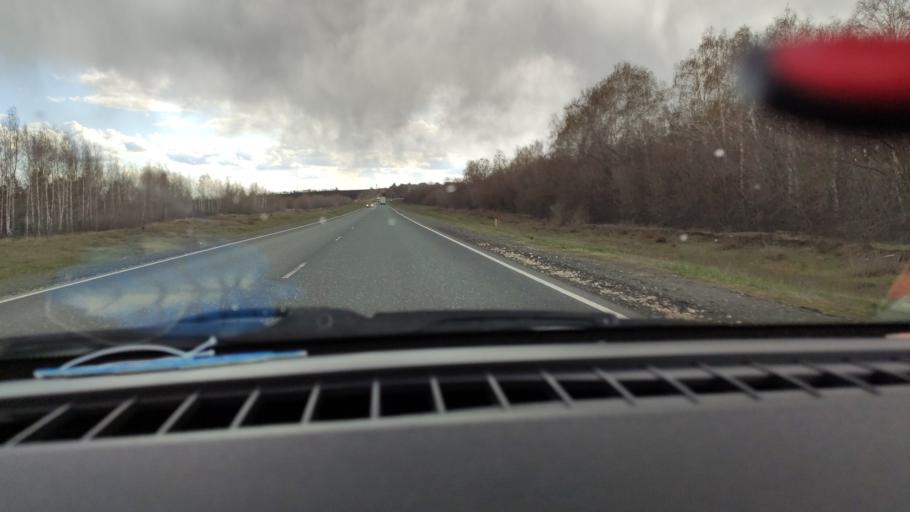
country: RU
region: Saratov
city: Balakovo
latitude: 52.1381
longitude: 47.7981
